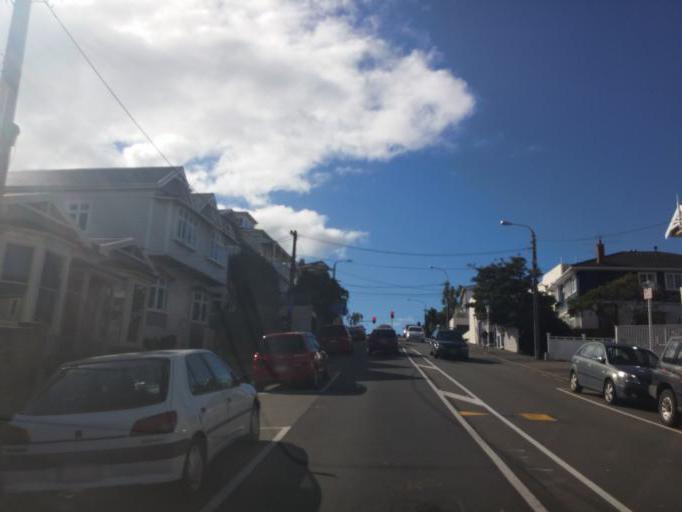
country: NZ
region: Wellington
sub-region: Wellington City
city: Wellington
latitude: -41.2897
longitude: 174.7716
